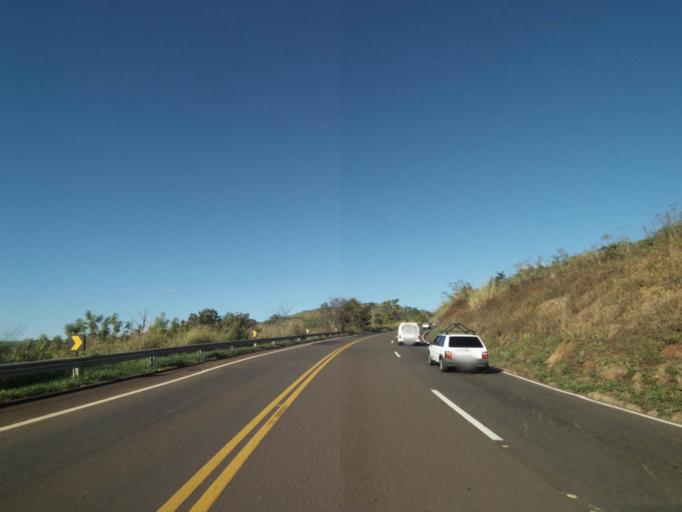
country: BR
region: Parana
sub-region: Londrina
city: Londrina
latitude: -23.6422
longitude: -51.1029
